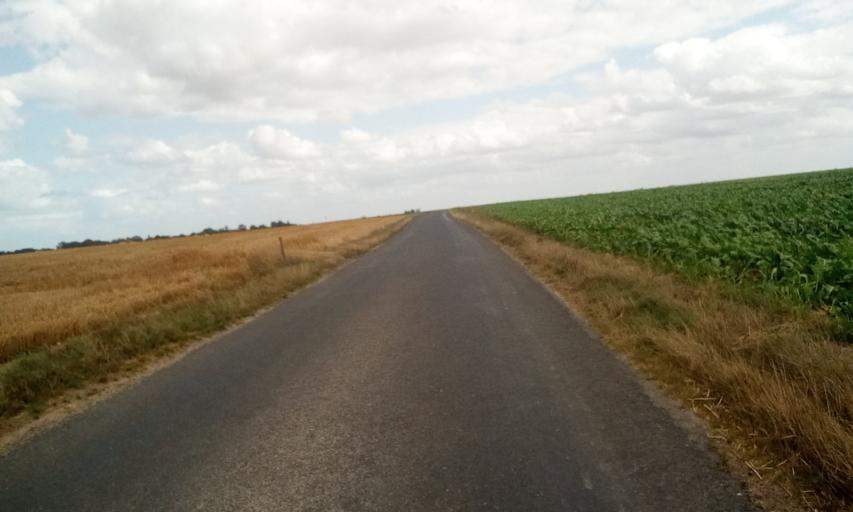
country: FR
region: Lower Normandy
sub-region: Departement du Calvados
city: Ver-sur-Mer
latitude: 49.3136
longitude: -0.5377
